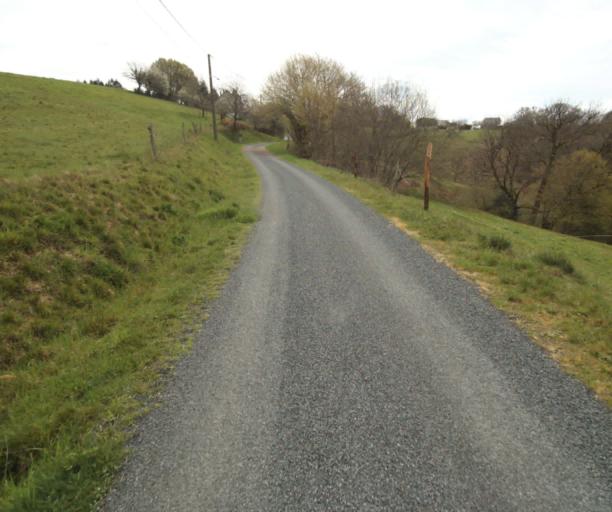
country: FR
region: Limousin
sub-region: Departement de la Correze
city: Sainte-Fortunade
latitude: 45.2040
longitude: 1.8534
